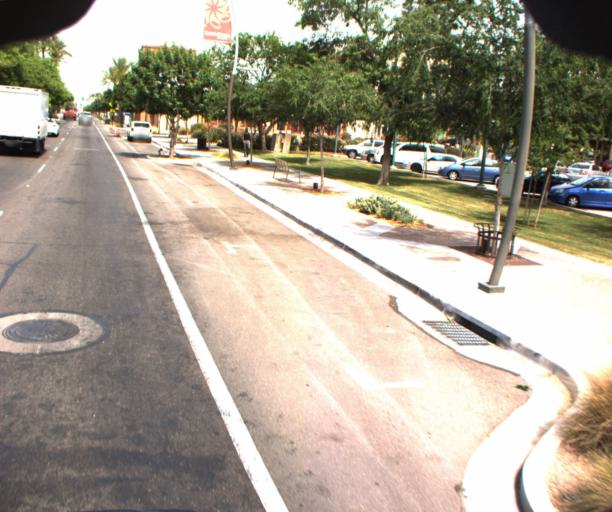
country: US
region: Arizona
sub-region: Maricopa County
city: Chandler
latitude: 33.3025
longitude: -111.8414
